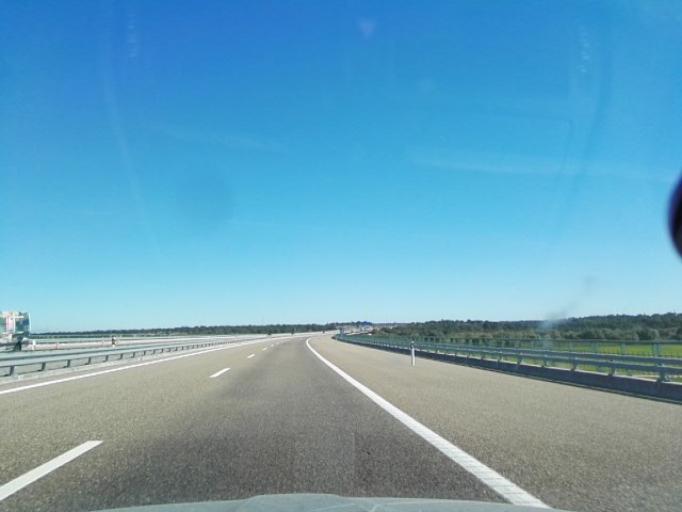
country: PT
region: Santarem
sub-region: Benavente
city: Poceirao
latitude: 38.8883
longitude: -8.7928
